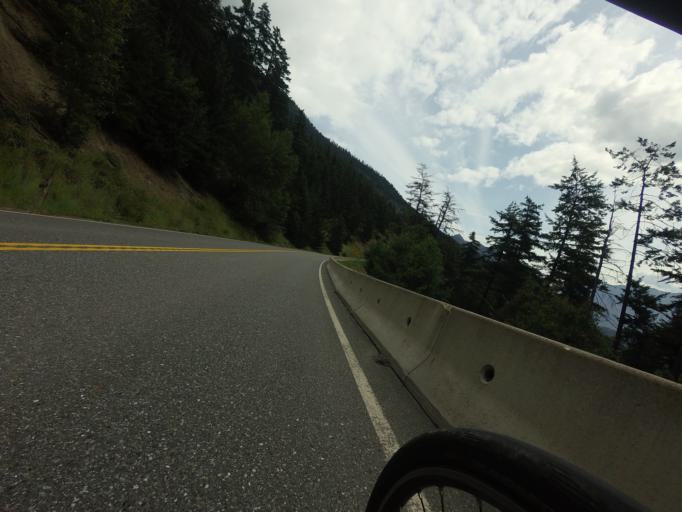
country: CA
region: British Columbia
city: Lillooet
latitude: 50.6473
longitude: -122.0224
